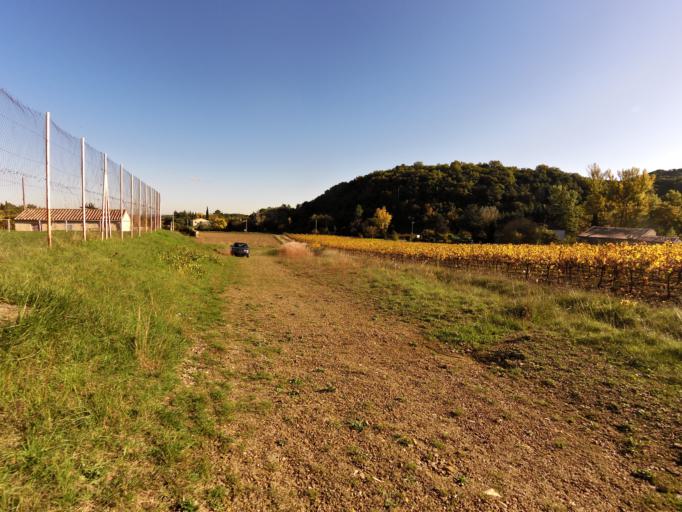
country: FR
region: Languedoc-Roussillon
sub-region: Departement du Gard
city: Sauve
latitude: 43.9902
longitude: 3.9475
